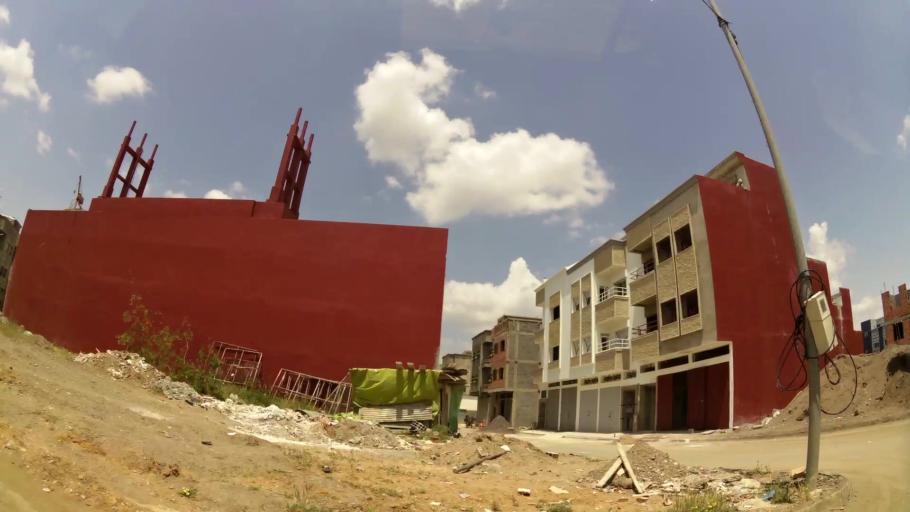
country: MA
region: Rabat-Sale-Zemmour-Zaer
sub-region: Khemisset
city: Tiflet
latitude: 34.0111
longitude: -6.5261
